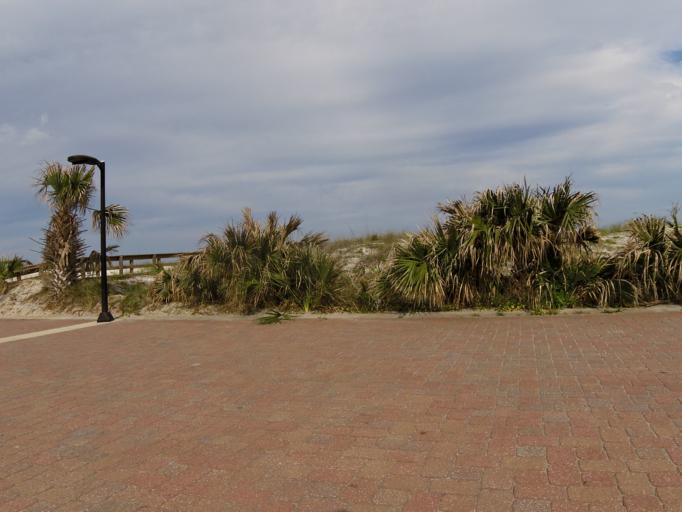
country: US
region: Florida
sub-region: Duval County
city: Jacksonville Beach
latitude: 30.2903
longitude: -81.3893
